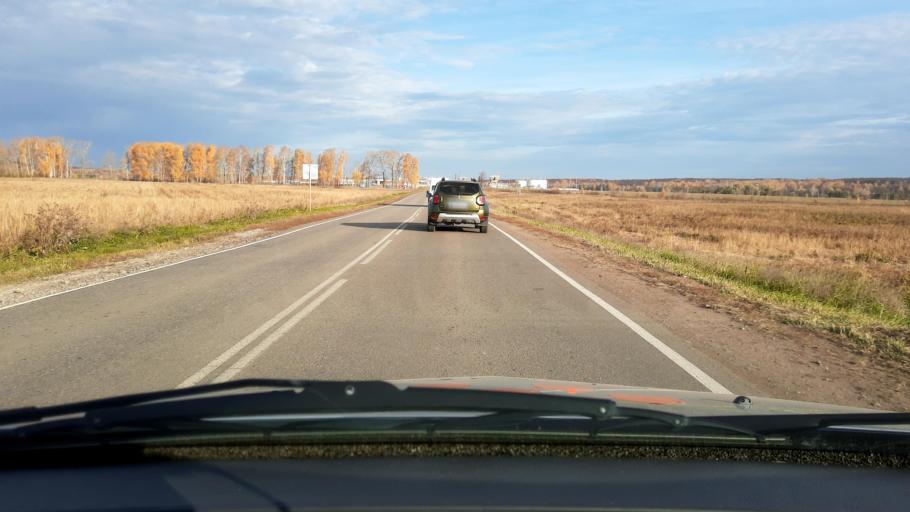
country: RU
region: Bashkortostan
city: Mikhaylovka
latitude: 54.8181
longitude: 55.7675
